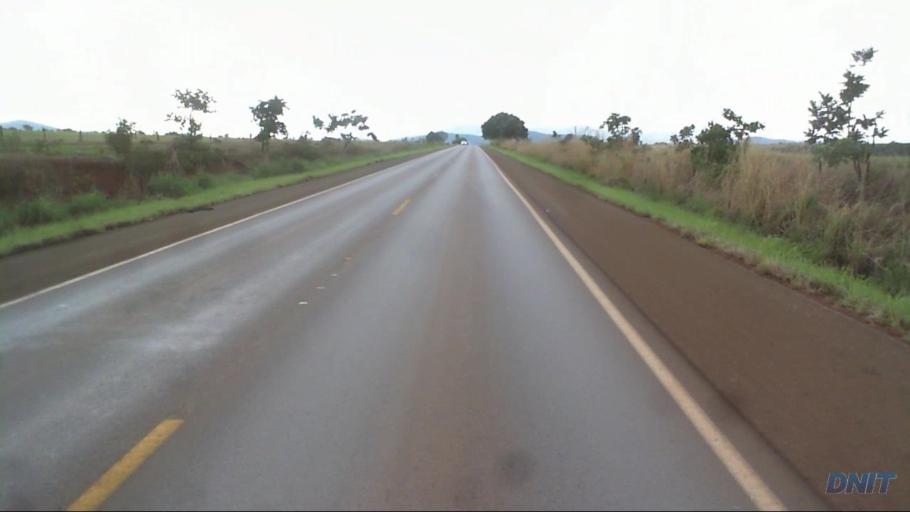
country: BR
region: Goias
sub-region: Barro Alto
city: Barro Alto
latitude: -14.8471
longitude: -49.0271
